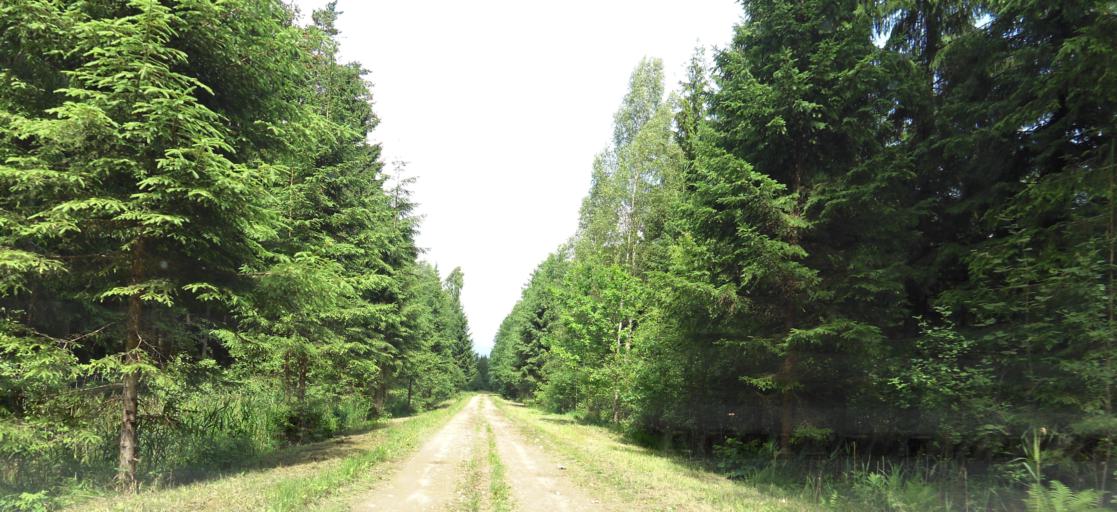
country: LT
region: Panevezys
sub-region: Birzai
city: Birzai
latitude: 56.2696
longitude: 24.7502
